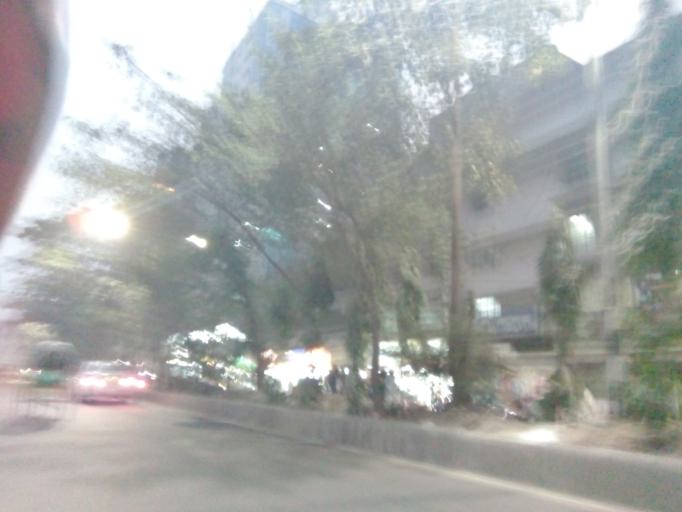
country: BD
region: Dhaka
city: Paltan
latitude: 23.7359
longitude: 90.4102
